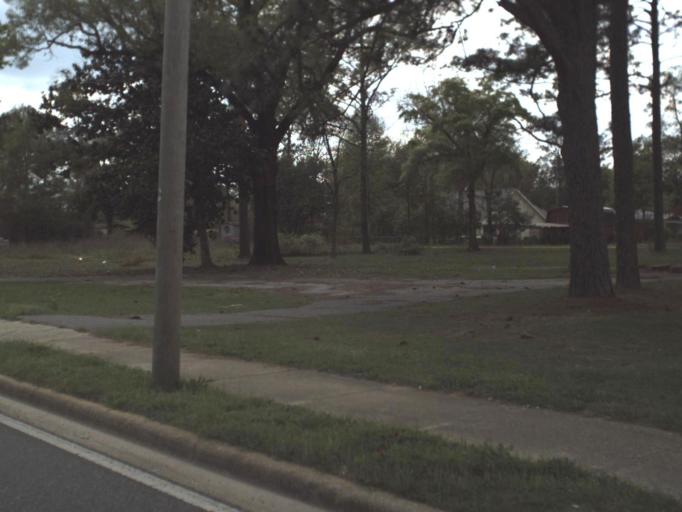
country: US
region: Florida
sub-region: Okaloosa County
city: Crestview
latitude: 30.7772
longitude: -86.5625
